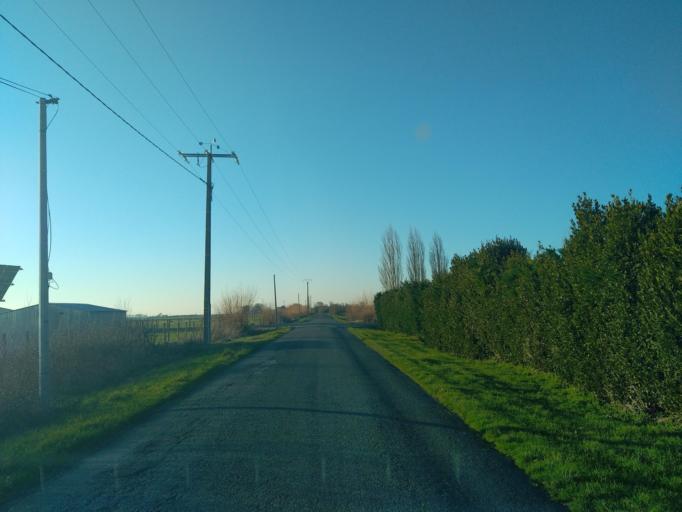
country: FR
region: Pays de la Loire
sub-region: Departement de la Vendee
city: Triaize
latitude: 46.3891
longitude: -1.2758
